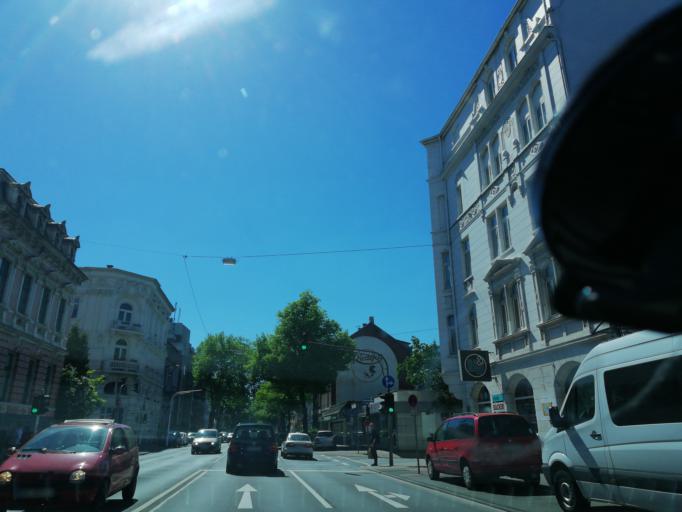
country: DE
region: North Rhine-Westphalia
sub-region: Regierungsbezirk Dusseldorf
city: Wuppertal
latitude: 51.2639
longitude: 7.1802
